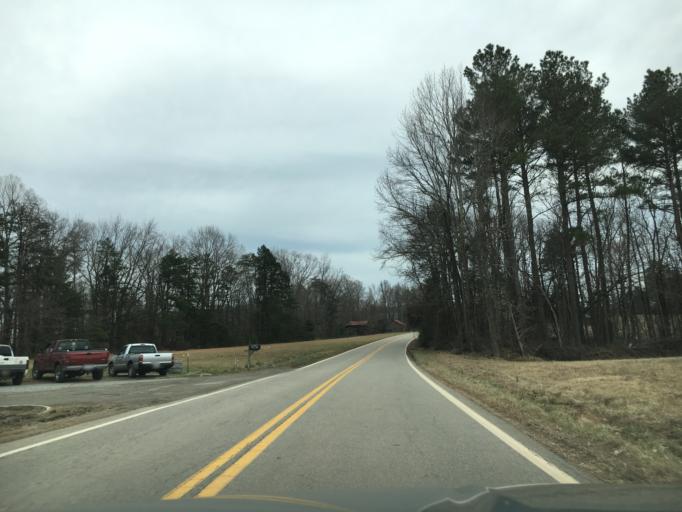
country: US
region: Virginia
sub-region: Charlotte County
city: Charlotte Court House
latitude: 36.9957
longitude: -78.6970
